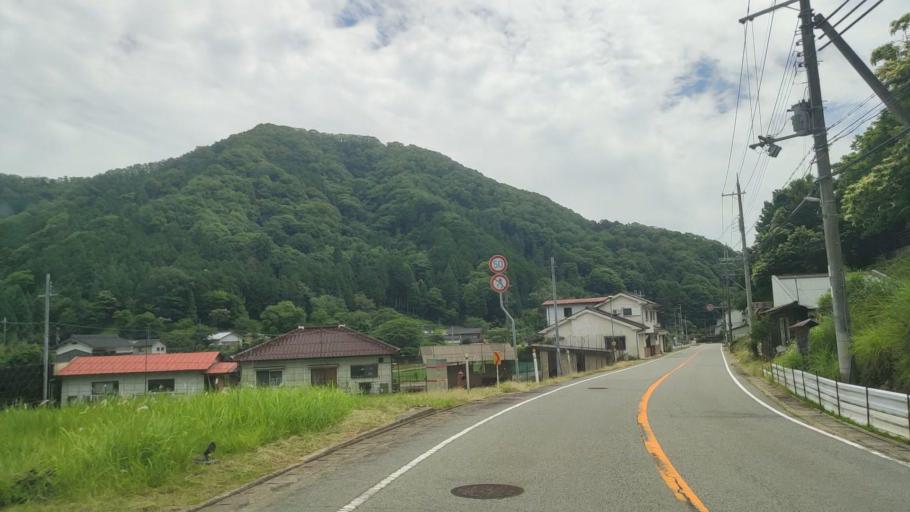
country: JP
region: Hyogo
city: Yamazakicho-nakabirose
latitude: 35.1013
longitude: 134.3629
